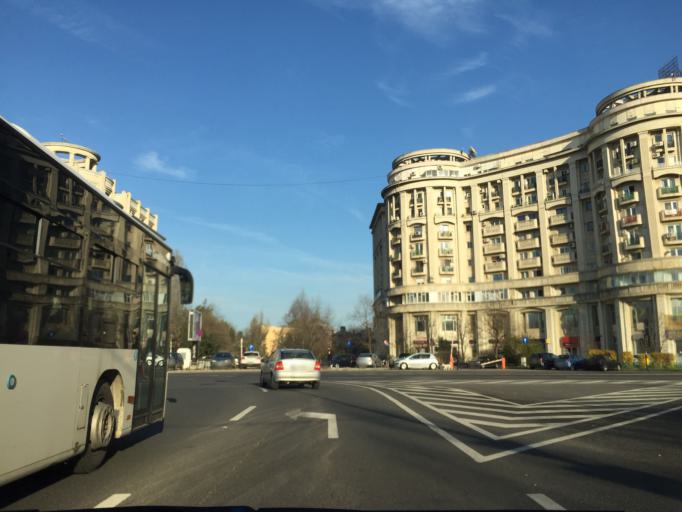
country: RO
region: Bucuresti
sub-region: Municipiul Bucuresti
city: Bucuresti
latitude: 44.4244
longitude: 26.0902
